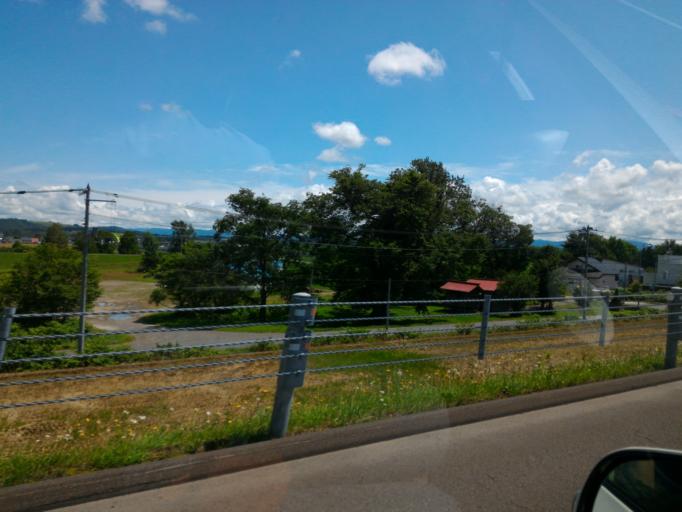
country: JP
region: Hokkaido
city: Nayoro
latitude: 44.3474
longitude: 142.4358
